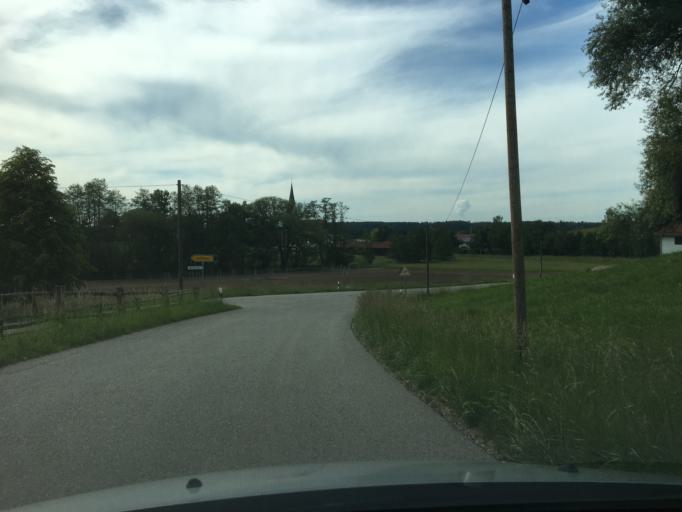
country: DE
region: Bavaria
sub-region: Upper Bavaria
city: Niedertaufkirchen
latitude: 48.3763
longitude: 12.5536
